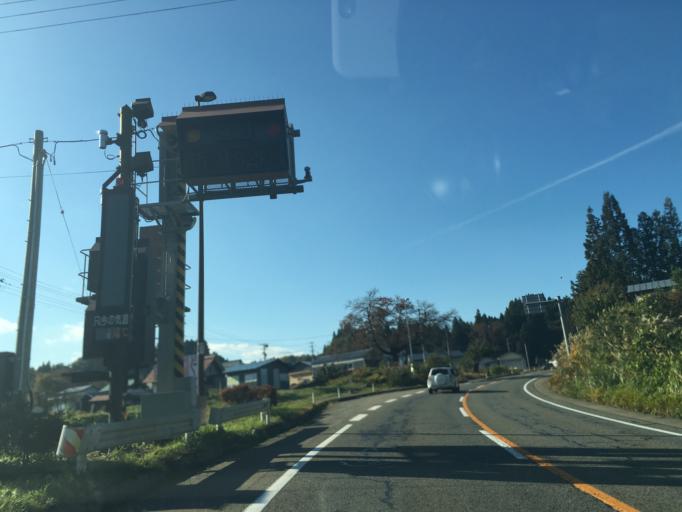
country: JP
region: Fukushima
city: Kitakata
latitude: 37.5559
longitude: 139.7516
